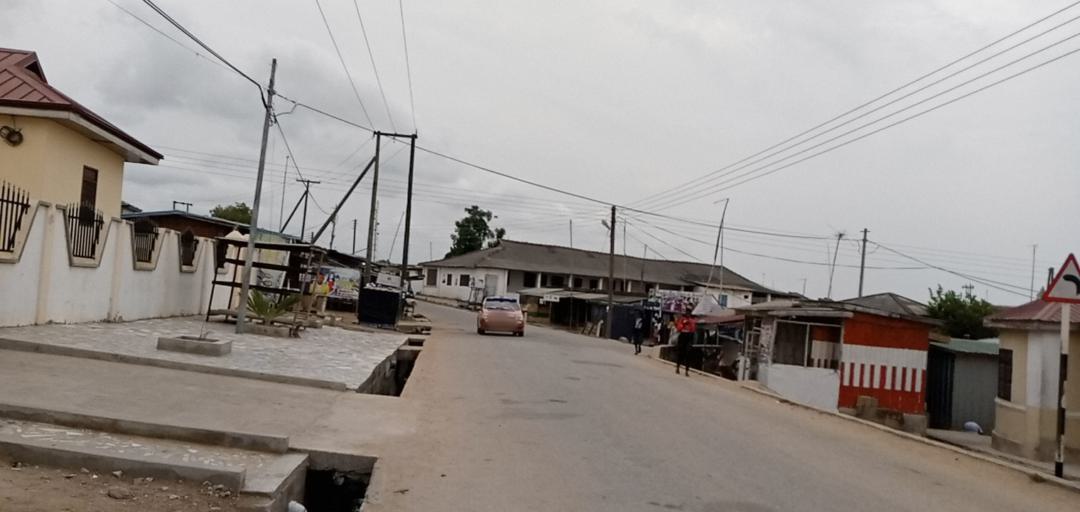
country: GH
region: Central
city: Winneba
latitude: 5.3472
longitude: -0.6214
